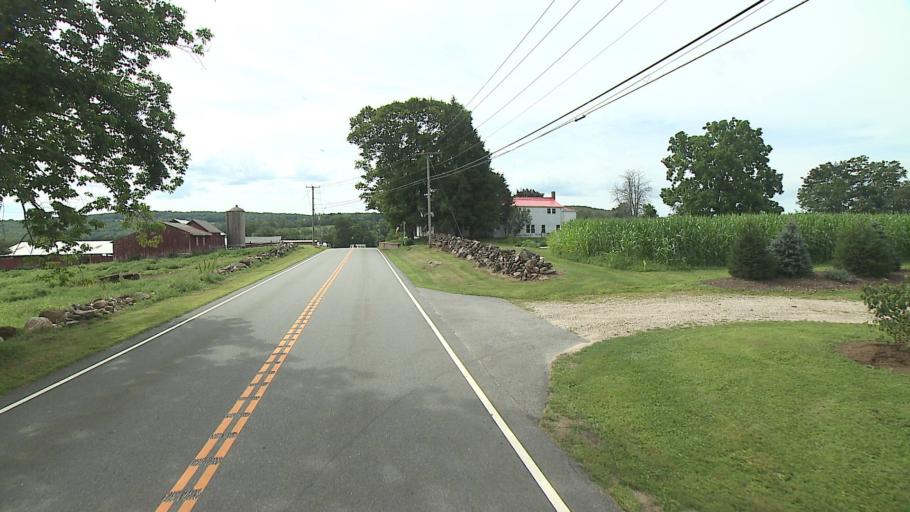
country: US
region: Connecticut
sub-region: Litchfield County
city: New Preston
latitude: 41.7234
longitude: -73.3358
